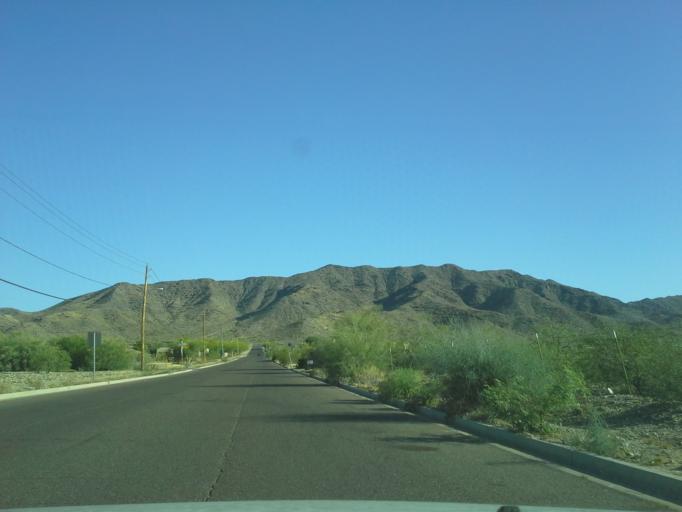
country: US
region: Arizona
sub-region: Maricopa County
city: Laveen
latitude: 33.3602
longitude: -112.1006
